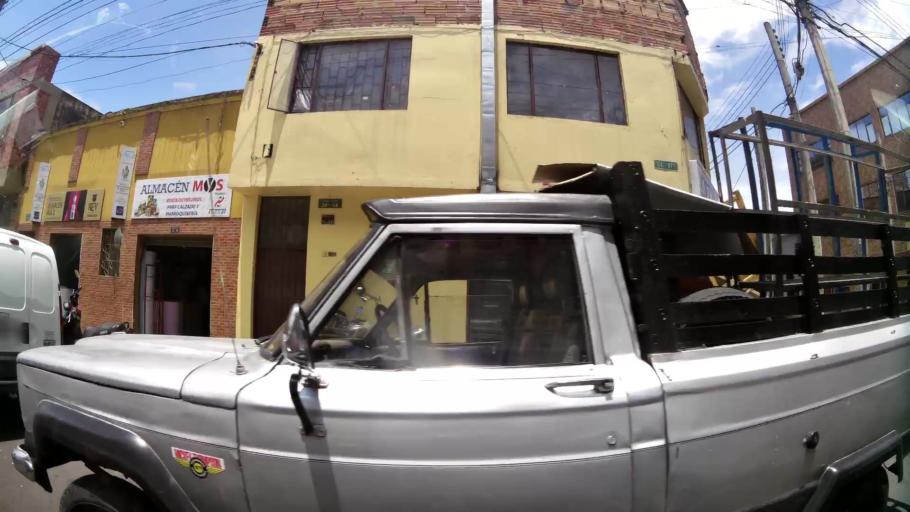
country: CO
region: Bogota D.C.
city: Bogota
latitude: 4.5889
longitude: -74.1038
